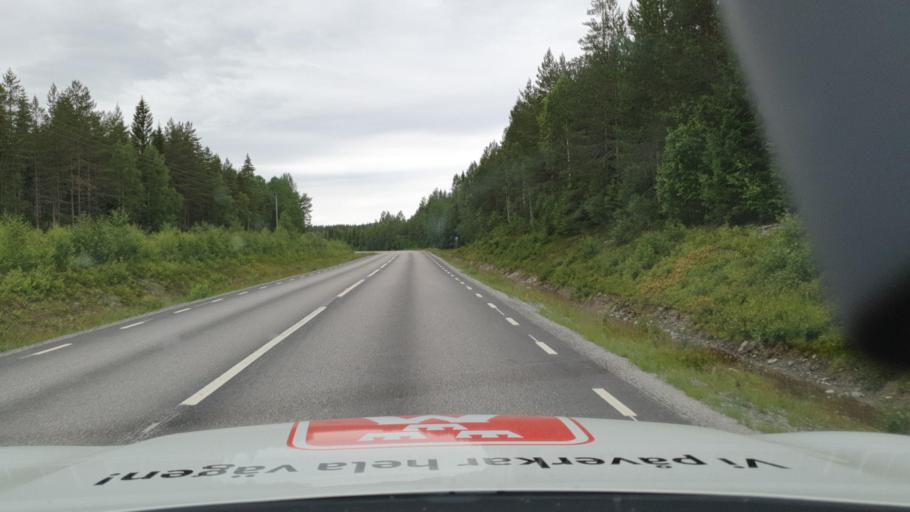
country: SE
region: Vaesterbotten
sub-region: Umea Kommun
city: Hoernefors
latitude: 63.7739
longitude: 19.9628
